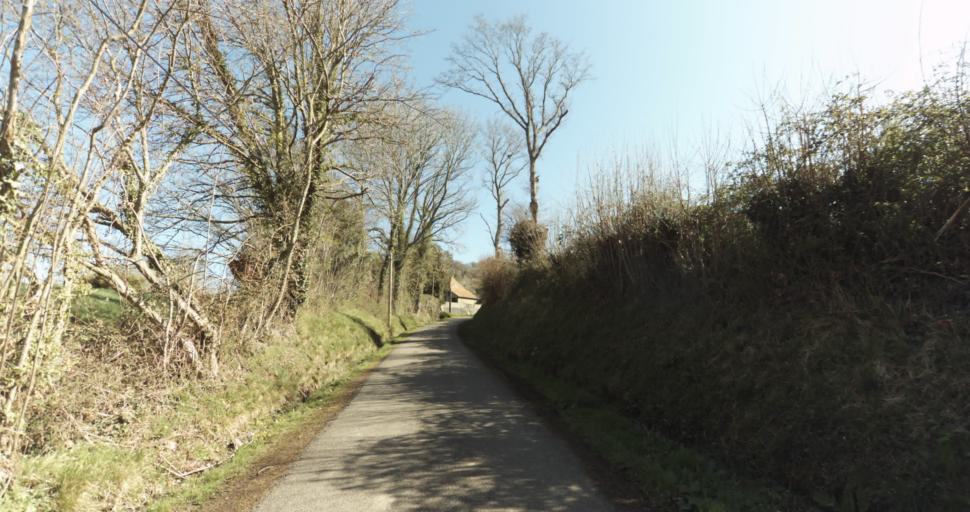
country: FR
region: Lower Normandy
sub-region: Departement du Calvados
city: Saint-Pierre-sur-Dives
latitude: 48.9898
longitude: 0.0401
